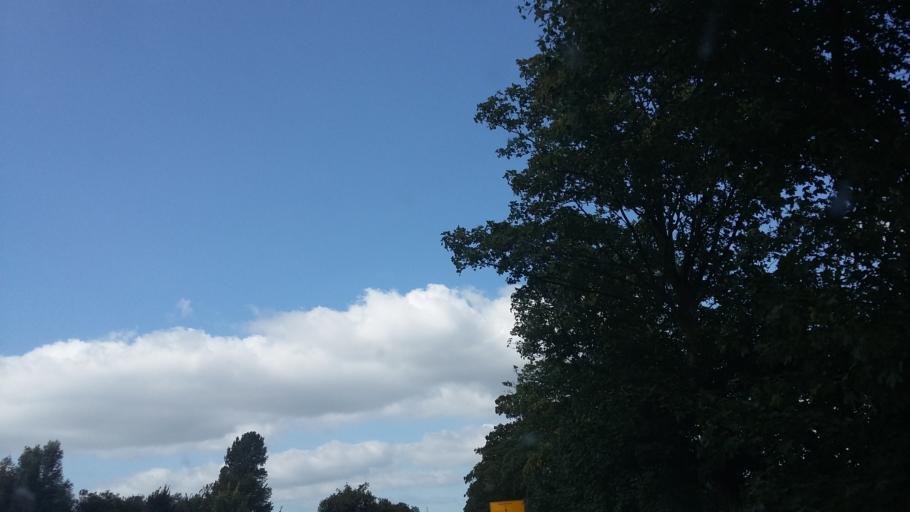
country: DE
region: Lower Saxony
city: Loxstedt
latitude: 53.4823
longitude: 8.6025
